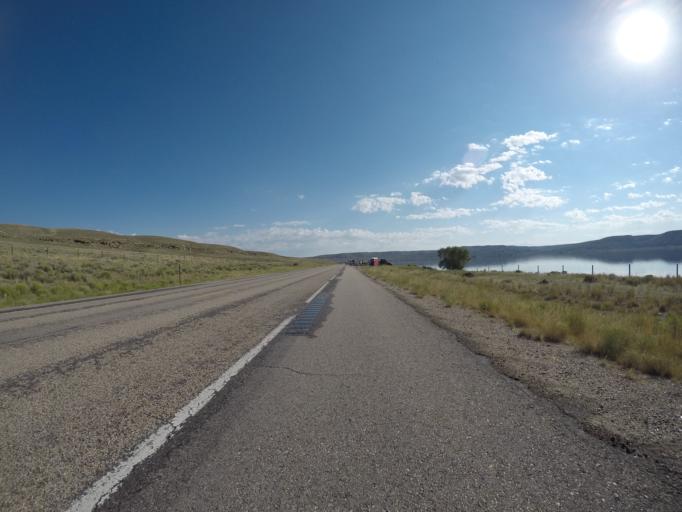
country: US
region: Wyoming
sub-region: Sublette County
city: Marbleton
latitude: 42.0992
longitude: -110.1439
